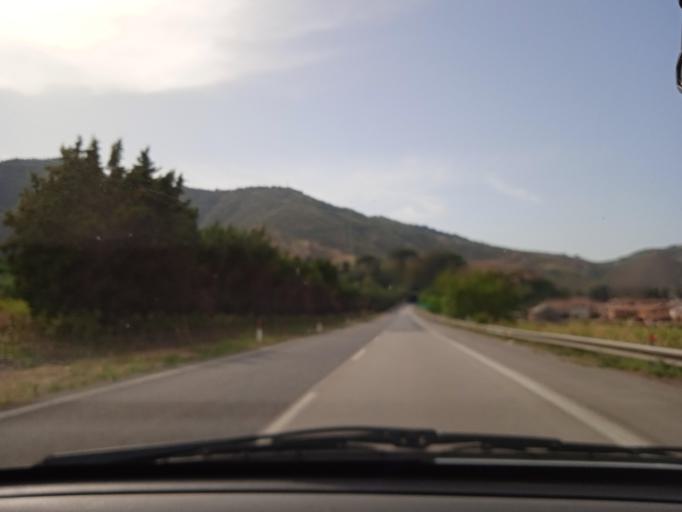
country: IT
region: Sicily
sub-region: Messina
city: Oliveri
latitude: 38.1189
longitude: 15.0598
